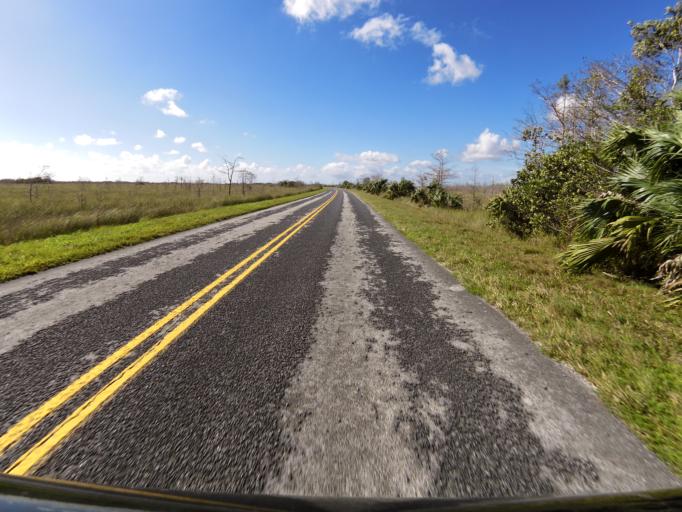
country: US
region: Florida
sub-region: Miami-Dade County
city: Florida City
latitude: 25.4334
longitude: -80.7568
